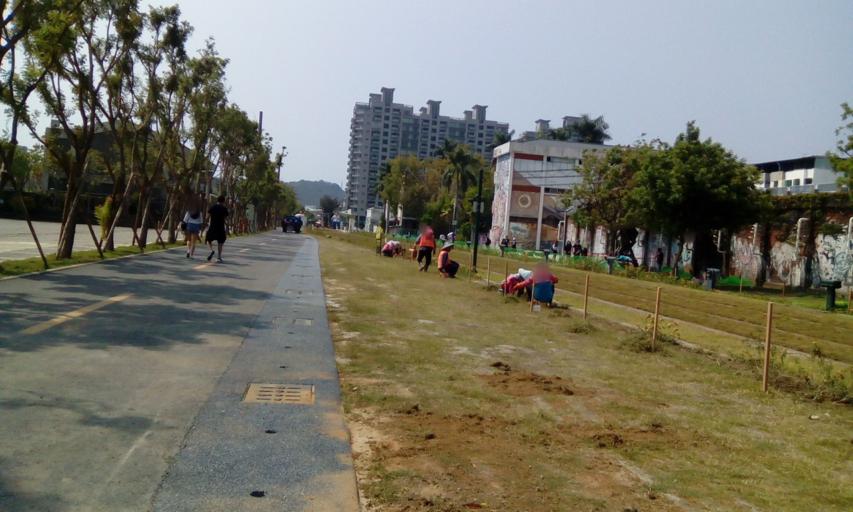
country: TW
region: Kaohsiung
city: Kaohsiung
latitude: 22.6197
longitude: 120.2815
